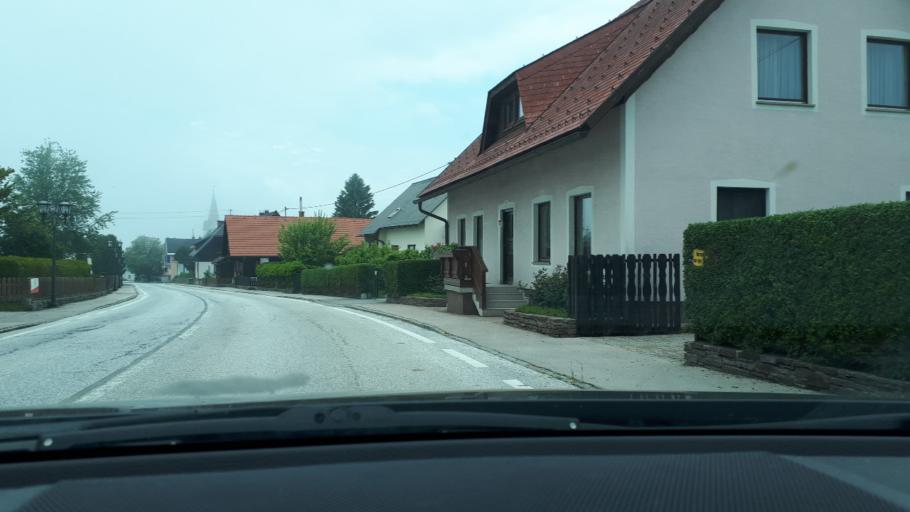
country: AT
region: Carinthia
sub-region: Politischer Bezirk Wolfsberg
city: Preitenegg
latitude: 46.9386
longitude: 14.9287
